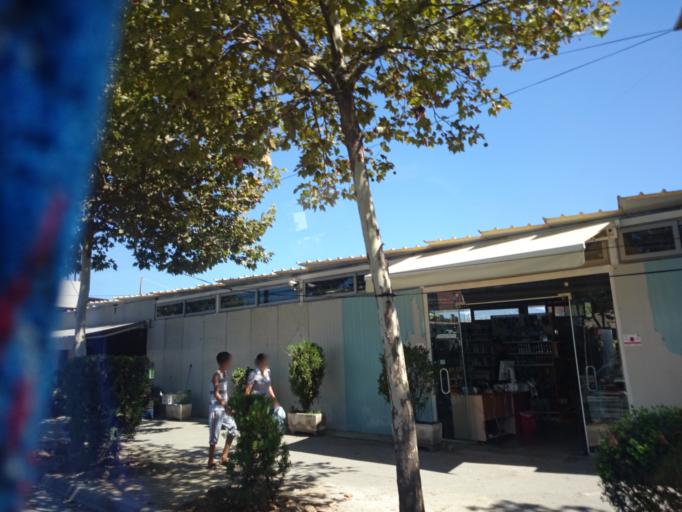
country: AL
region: Tirane
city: Tirana
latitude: 41.3251
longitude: 19.7877
